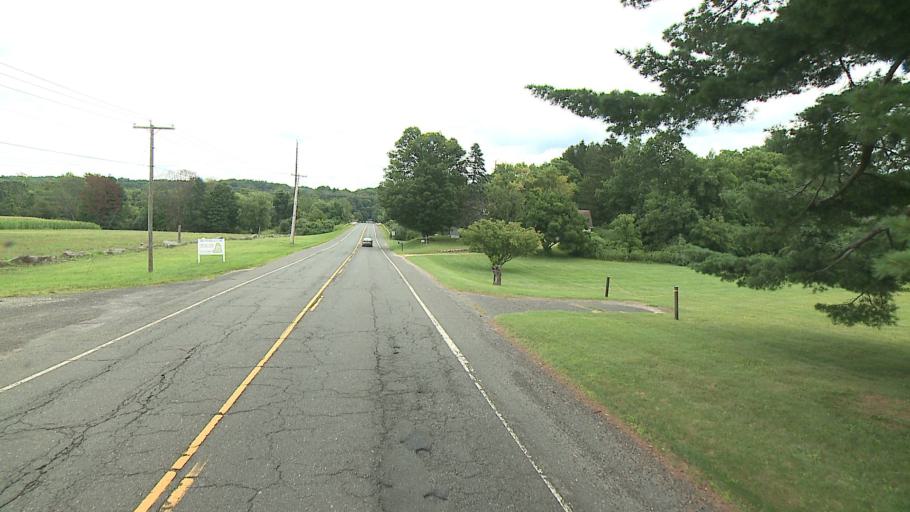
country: US
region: Connecticut
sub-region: Fairfield County
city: Danbury
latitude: 41.4556
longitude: -73.3999
